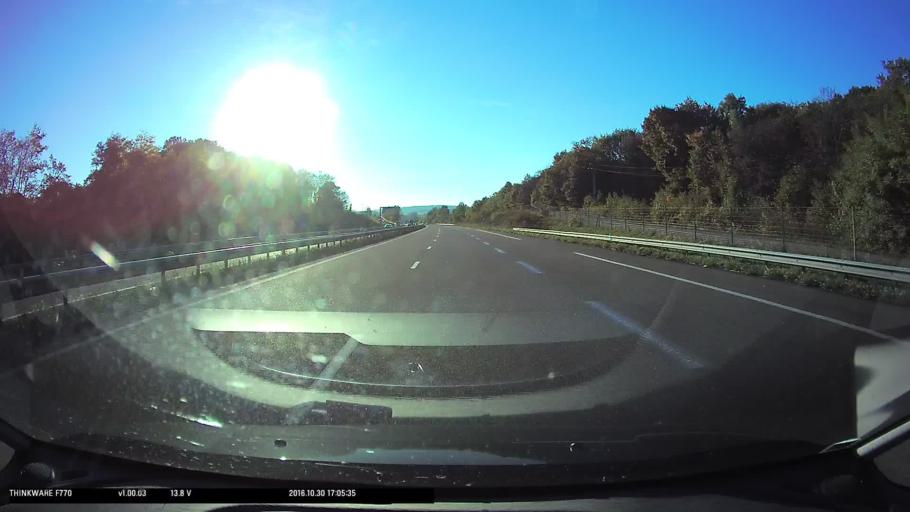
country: FR
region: Franche-Comte
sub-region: Departement du Jura
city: Orchamps
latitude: 47.1474
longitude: 5.5766
